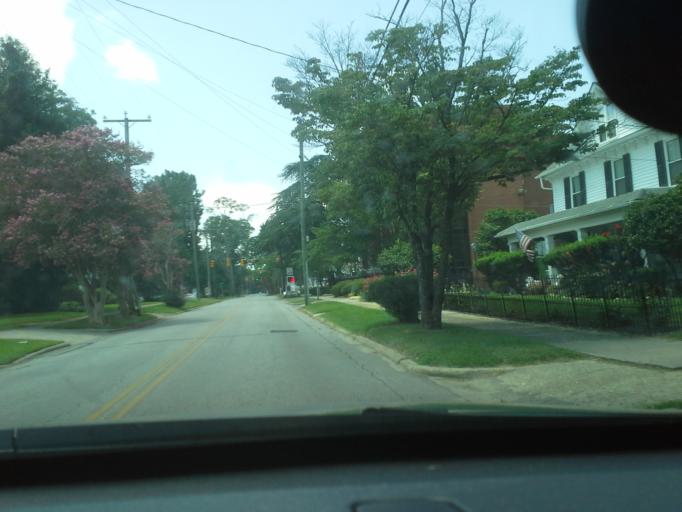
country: US
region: North Carolina
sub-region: Washington County
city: Plymouth
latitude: 35.8671
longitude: -76.7478
